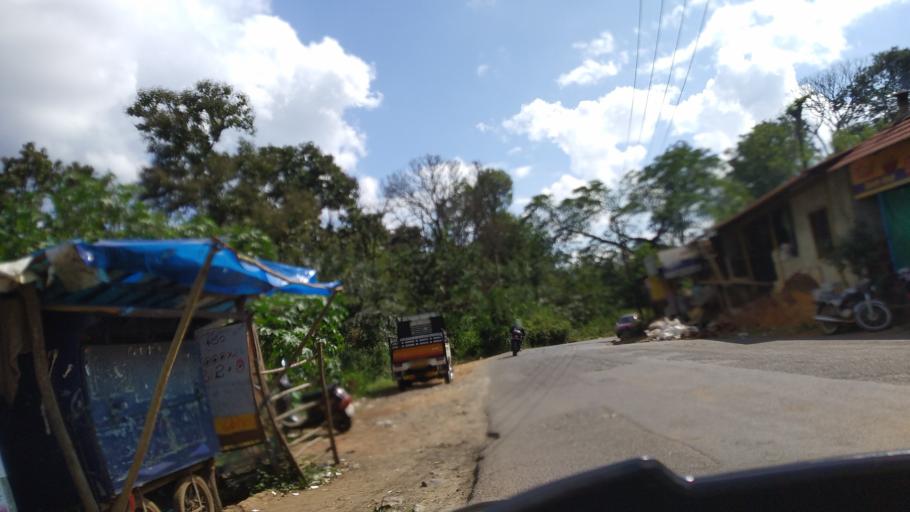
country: IN
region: Karnataka
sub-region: Kodagu
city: Ponnampet
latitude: 11.9571
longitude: 76.0629
